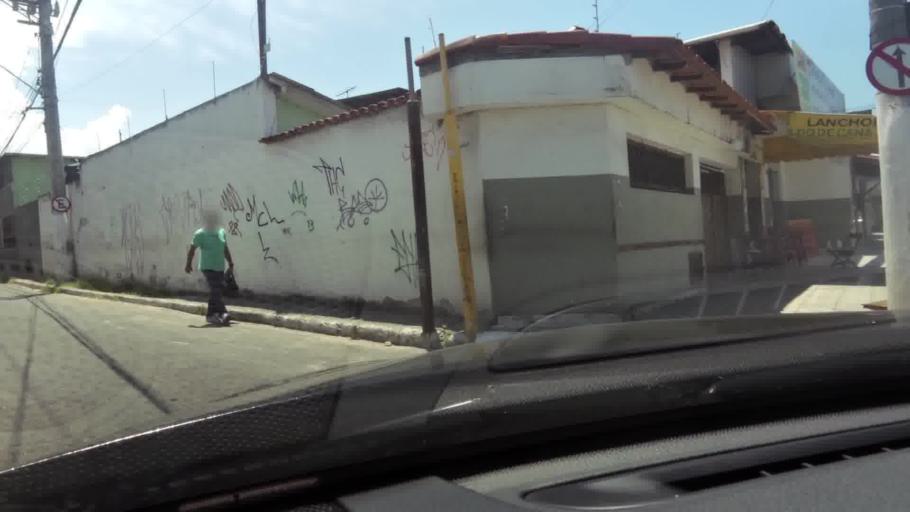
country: BR
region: Espirito Santo
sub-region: Viana
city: Viana
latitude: -20.4989
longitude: -40.3628
